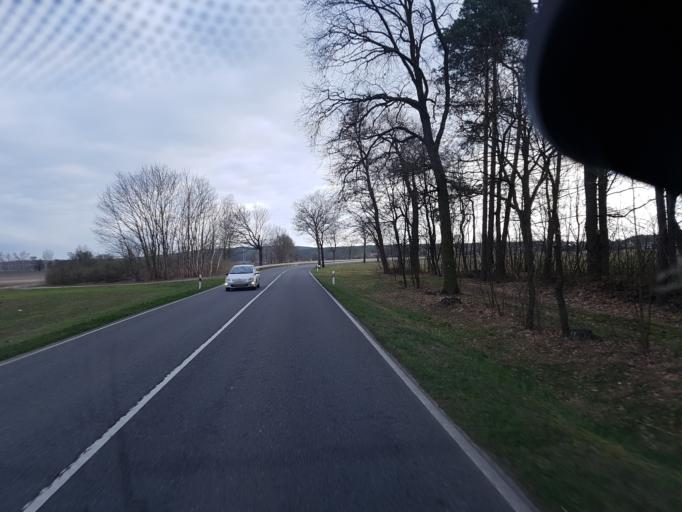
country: DE
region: Brandenburg
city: Schlepzig
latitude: 51.9819
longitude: 13.9643
